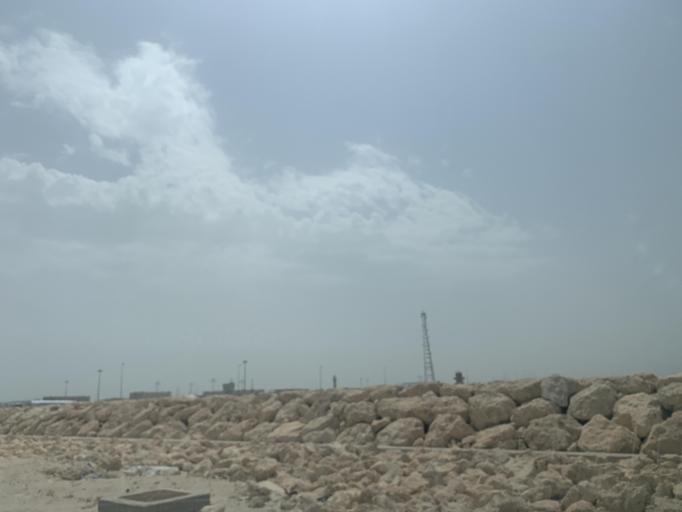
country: BH
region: Muharraq
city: Al Hadd
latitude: 26.2271
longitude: 50.7013
